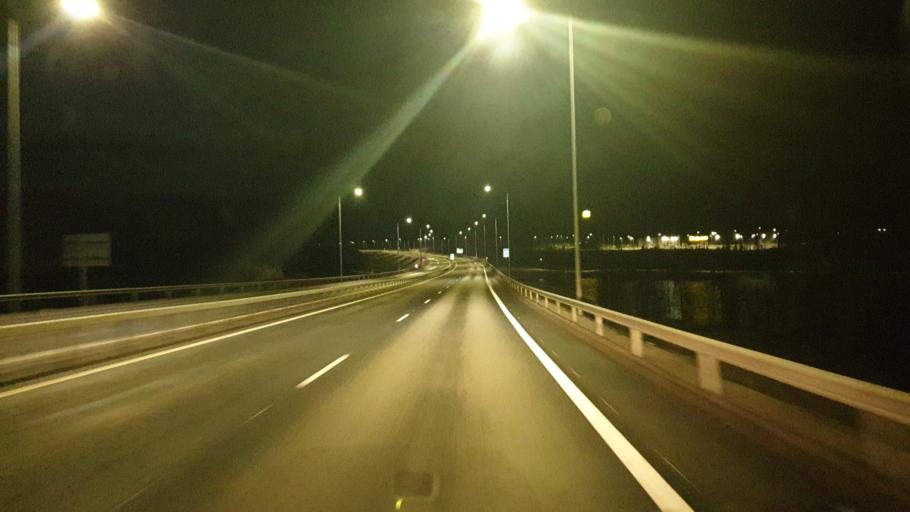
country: FI
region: Central Finland
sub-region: AEaenekoski
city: AEaenekoski
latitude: 62.6022
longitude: 25.6893
